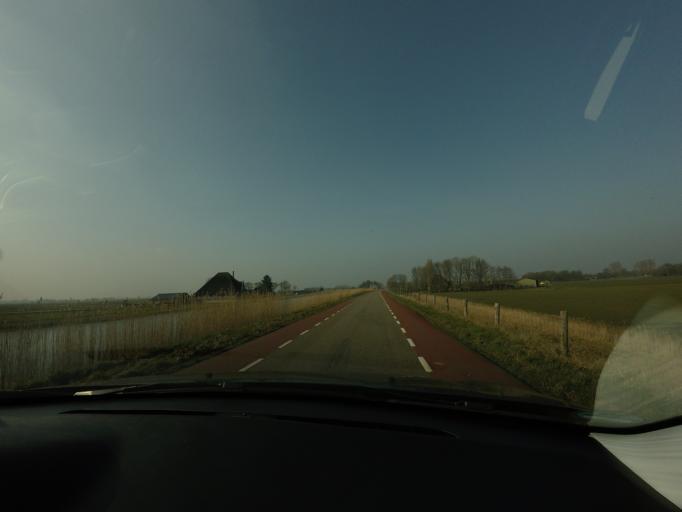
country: NL
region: North Holland
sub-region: Gemeente Opmeer
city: Opmeer
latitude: 52.6183
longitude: 4.9291
